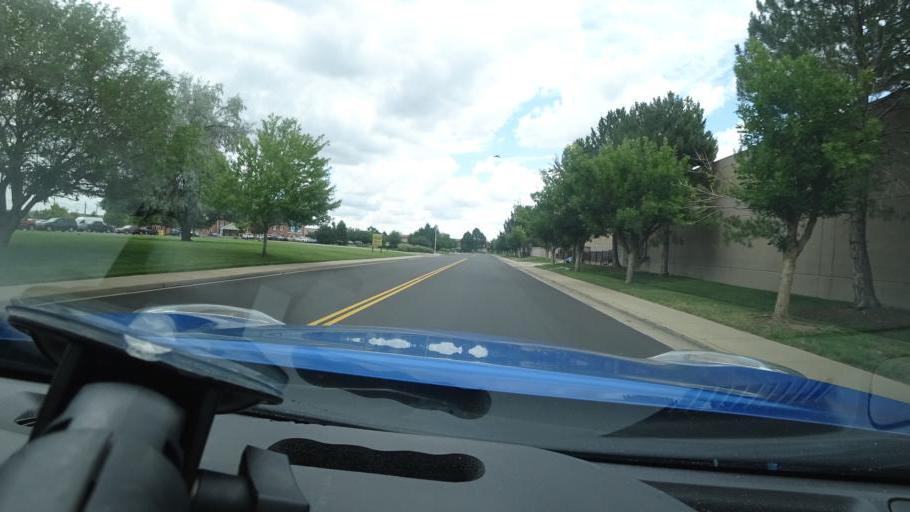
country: US
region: Colorado
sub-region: Adams County
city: Aurora
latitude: 39.7231
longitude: -104.8217
